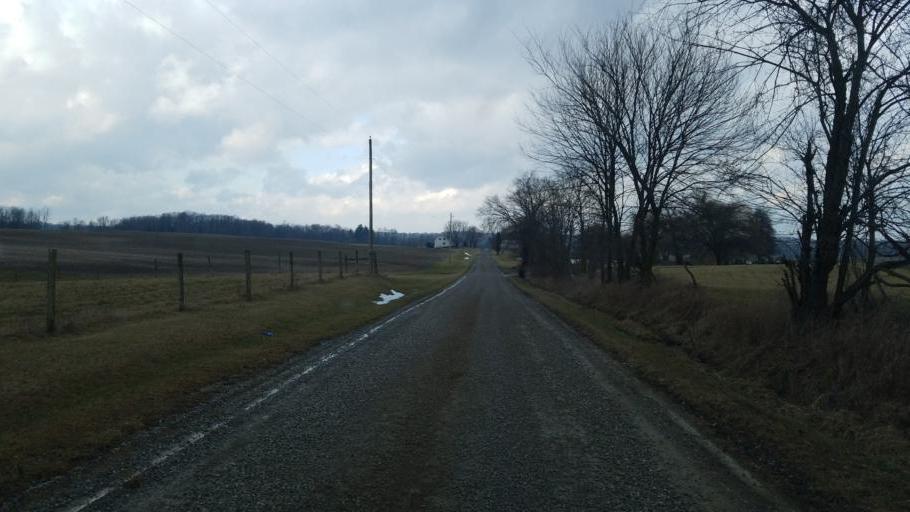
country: US
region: Ohio
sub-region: Morrow County
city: Mount Gilead
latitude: 40.5100
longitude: -82.6857
